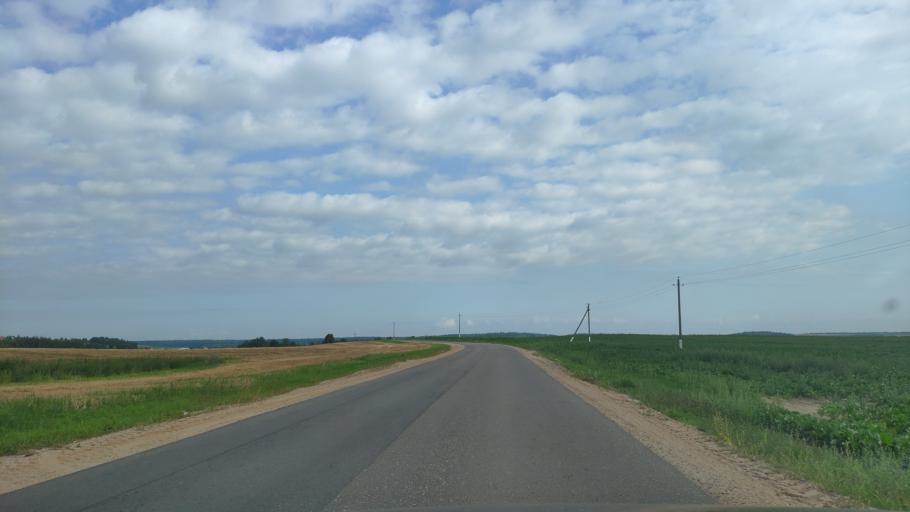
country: BY
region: Minsk
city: Khatsyezhyna
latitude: 53.8441
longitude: 27.3134
